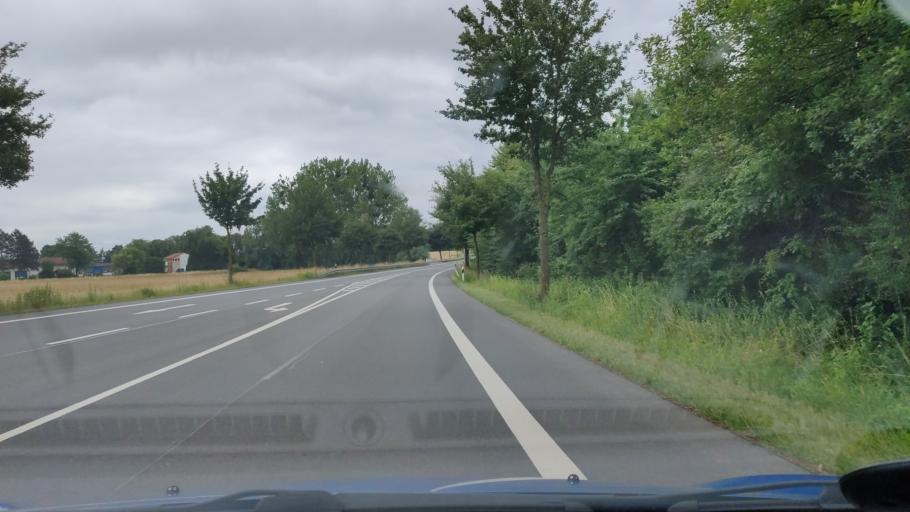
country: DE
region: Lower Saxony
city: Dielmissen
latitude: 51.9675
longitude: 9.5991
